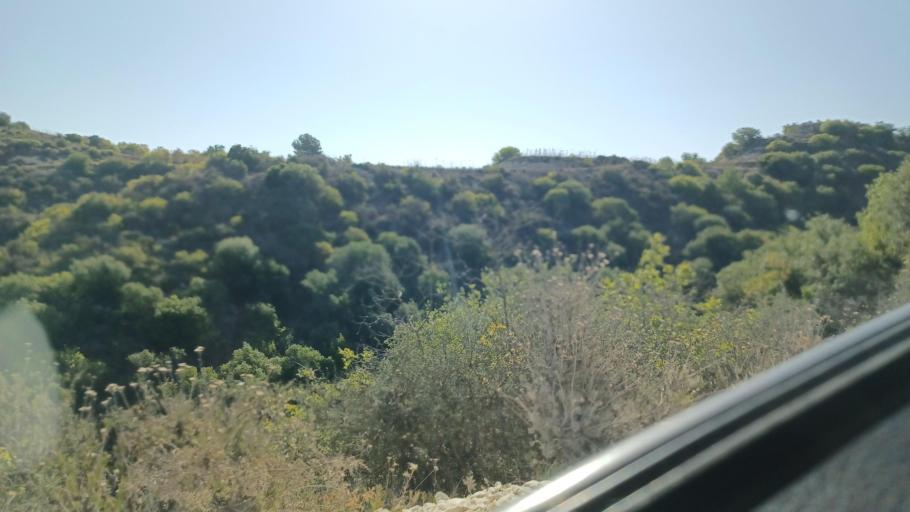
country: CY
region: Pafos
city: Tala
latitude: 34.8695
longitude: 32.4483
